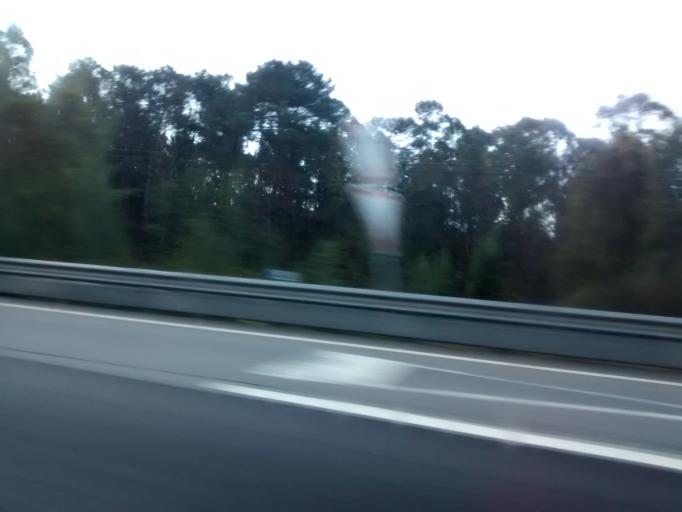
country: PT
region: Viseu
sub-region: Oliveira de Frades
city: Oliveira de Frades
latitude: 40.6823
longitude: -8.1972
